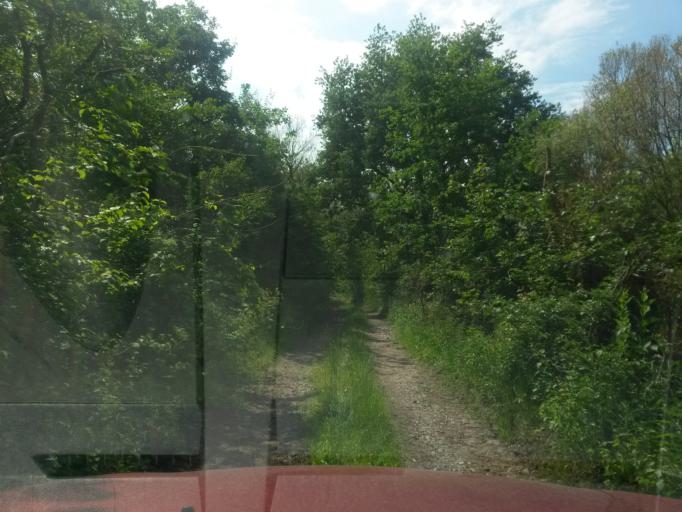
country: SK
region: Kosicky
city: Secovce
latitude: 48.6279
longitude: 21.4970
